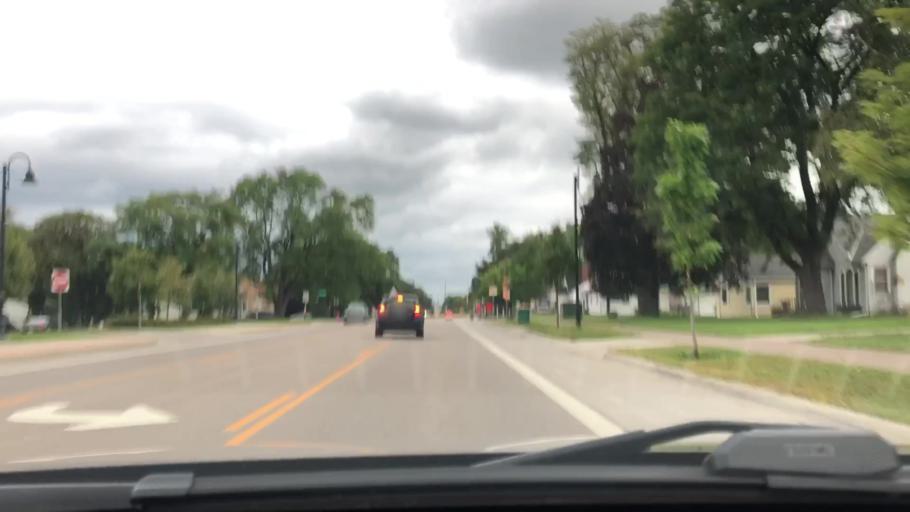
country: US
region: Minnesota
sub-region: Hennepin County
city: Richfield
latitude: 44.8811
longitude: -93.2679
